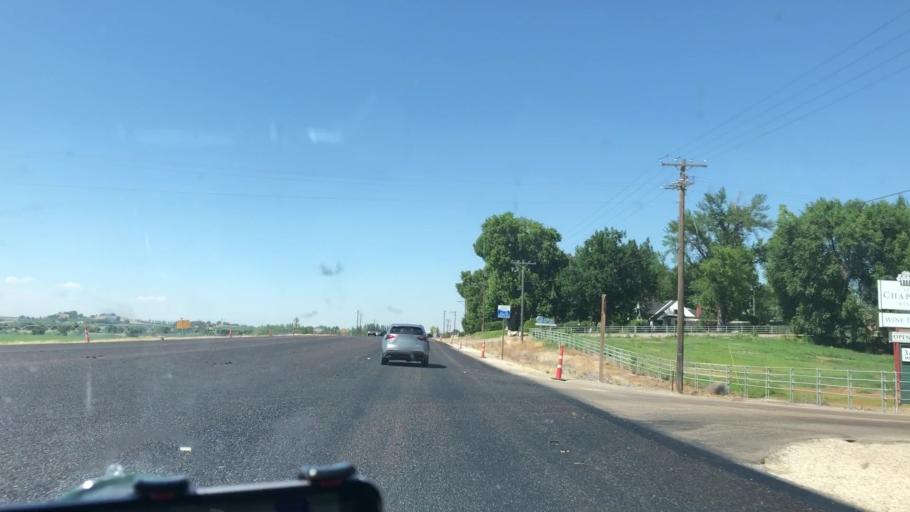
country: US
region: Idaho
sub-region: Owyhee County
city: Marsing
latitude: 43.5740
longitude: -116.7924
